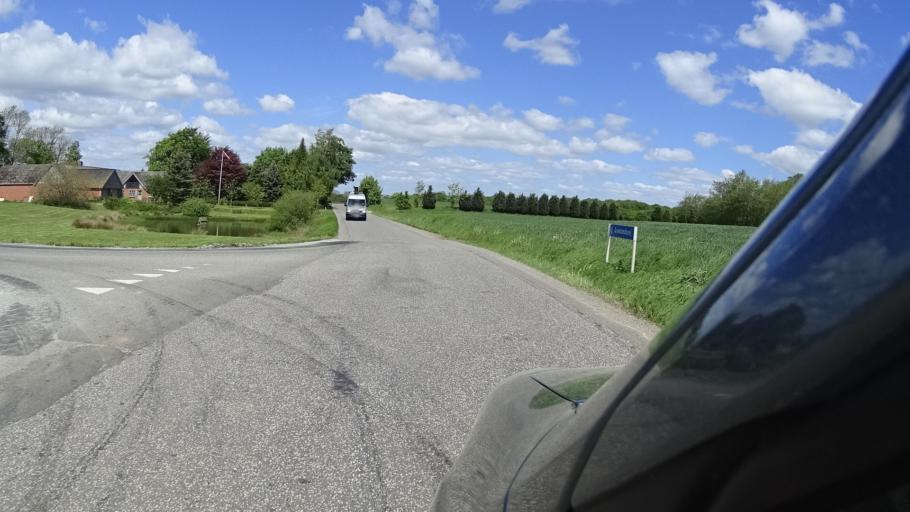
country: DK
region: South Denmark
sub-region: Vejle Kommune
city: Vejle
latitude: 55.6516
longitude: 9.5446
